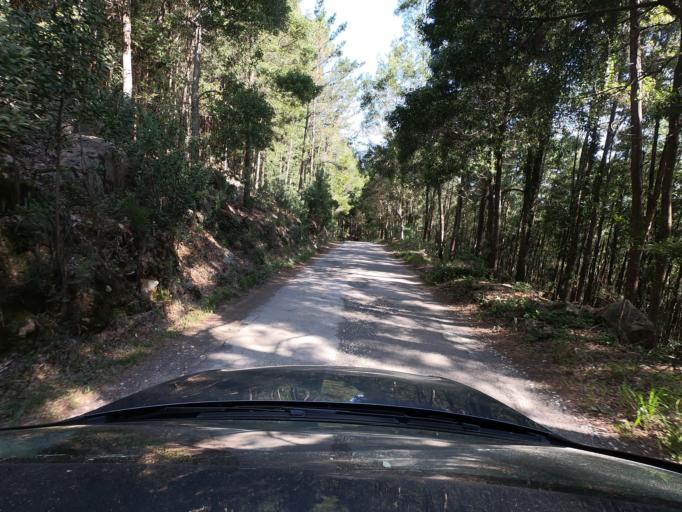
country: PT
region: Lisbon
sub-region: Sintra
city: Colares
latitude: 38.7764
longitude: -9.4373
